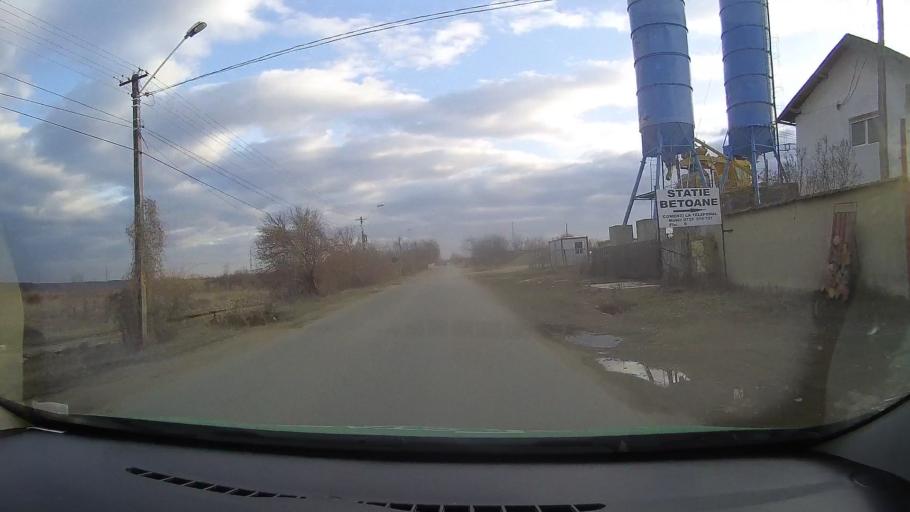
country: RO
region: Dambovita
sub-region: Comuna I. L. Caragiale
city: Ghirdoveni
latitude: 44.9603
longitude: 25.6573
